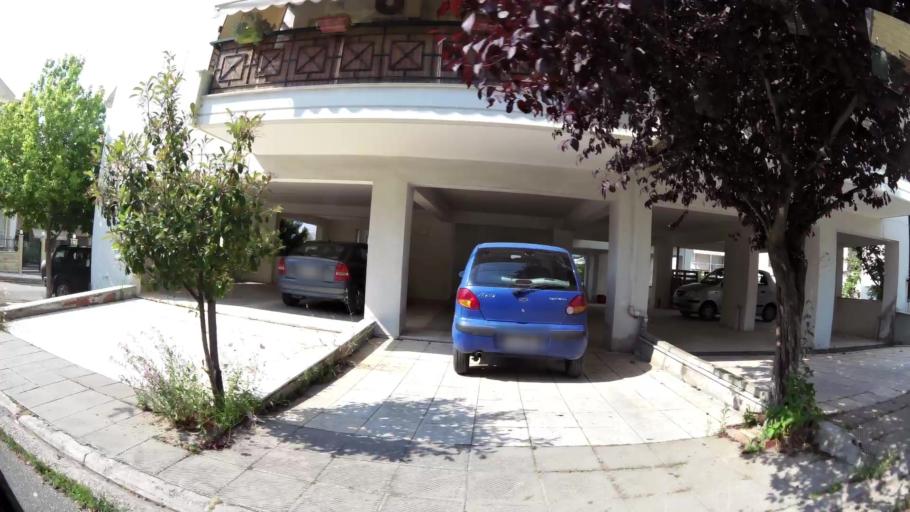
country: GR
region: Central Macedonia
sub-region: Nomos Thessalonikis
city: Polichni
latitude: 40.6690
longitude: 22.9493
